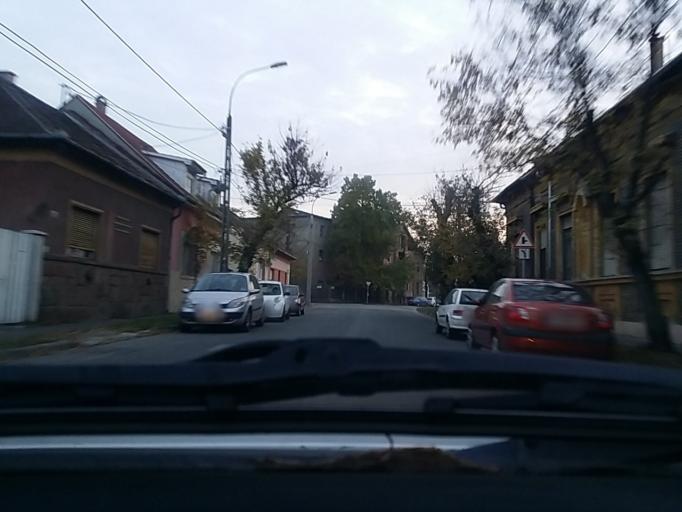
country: HU
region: Budapest
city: Budapest XV. keruelet
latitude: 47.5496
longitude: 19.1069
